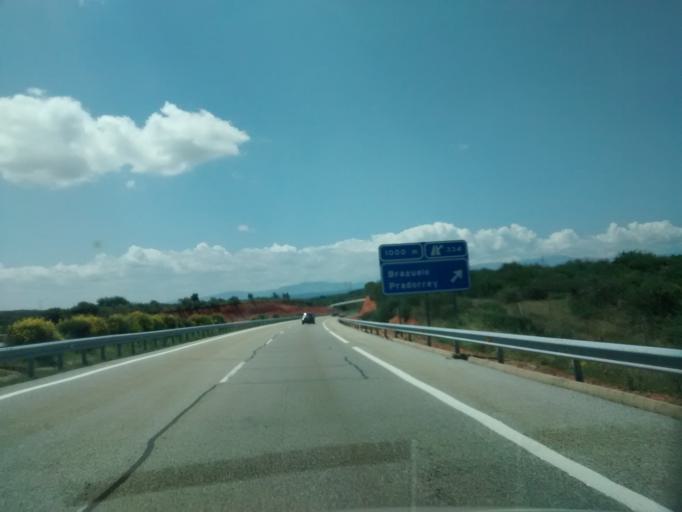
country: ES
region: Castille and Leon
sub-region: Provincia de Leon
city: Brazuelo
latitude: 42.5031
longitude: -6.1197
